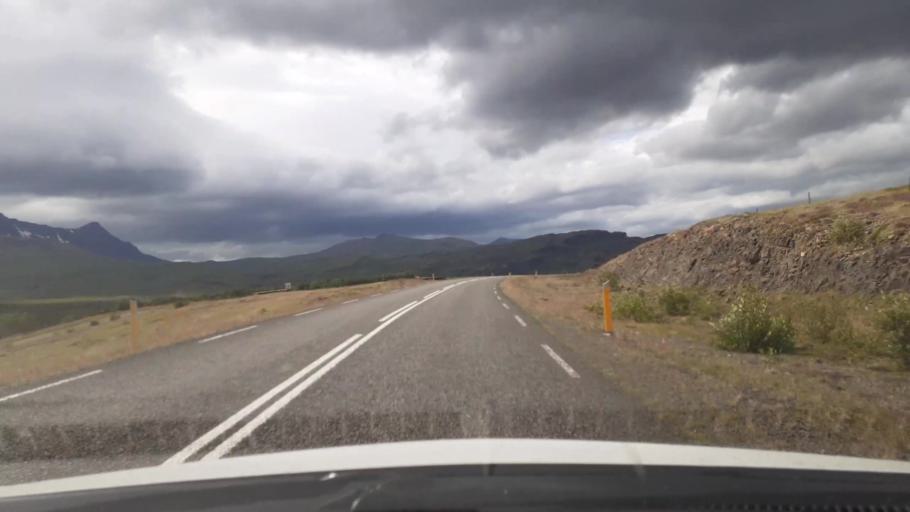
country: IS
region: West
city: Borgarnes
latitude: 64.5458
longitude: -21.6560
